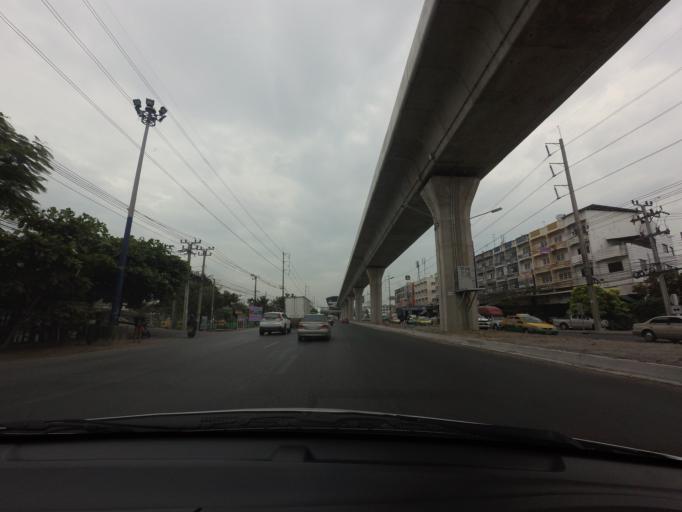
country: TH
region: Samut Prakan
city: Samut Prakan
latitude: 13.5705
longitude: 100.6065
